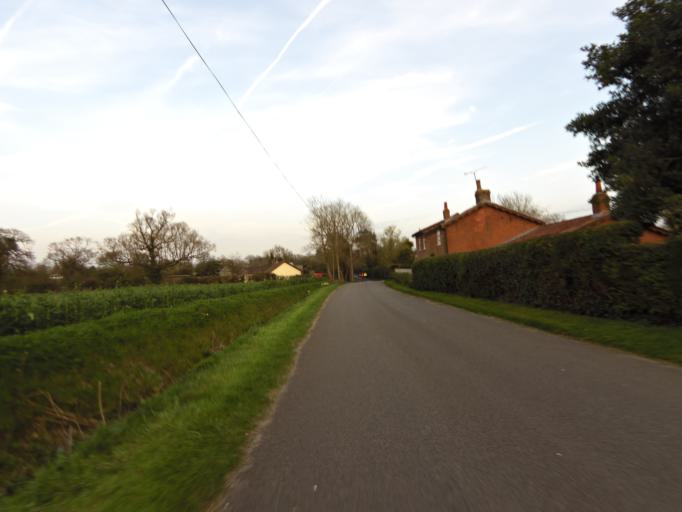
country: GB
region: England
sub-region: Suffolk
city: Debenham
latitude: 52.1545
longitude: 1.2122
